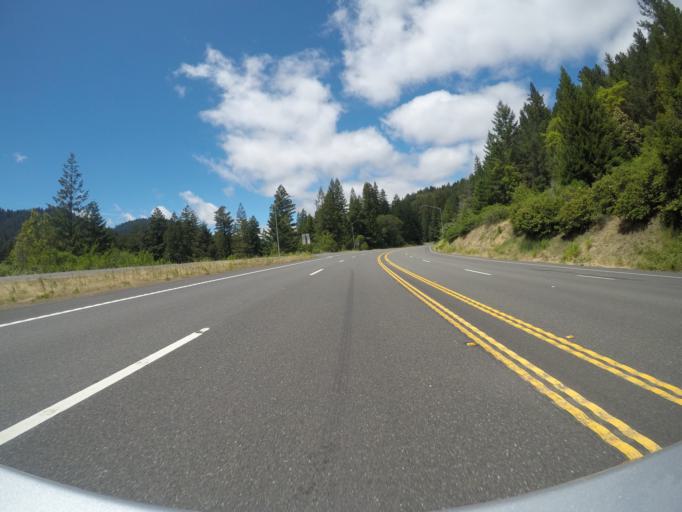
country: US
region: California
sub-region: Humboldt County
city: Redway
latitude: 40.2680
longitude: -123.8733
